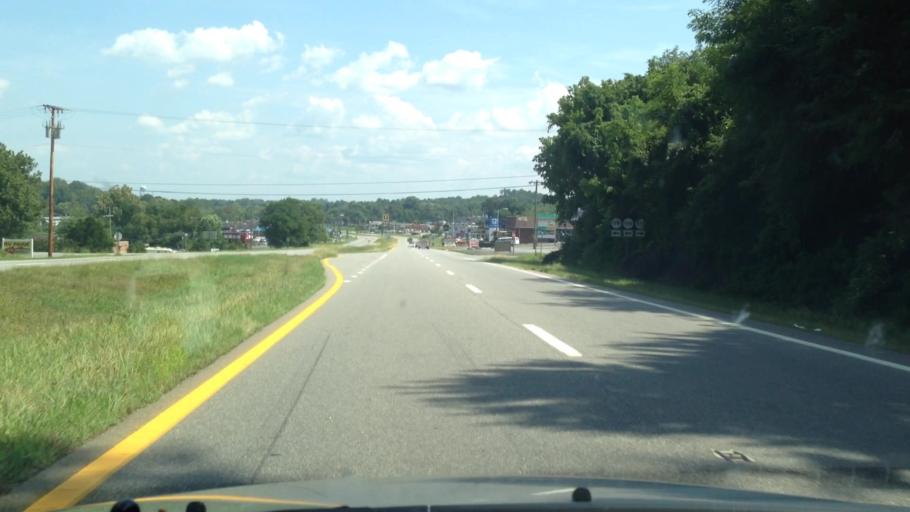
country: US
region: Virginia
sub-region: City of Martinsville
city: Martinsville
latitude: 36.6584
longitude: -79.8802
